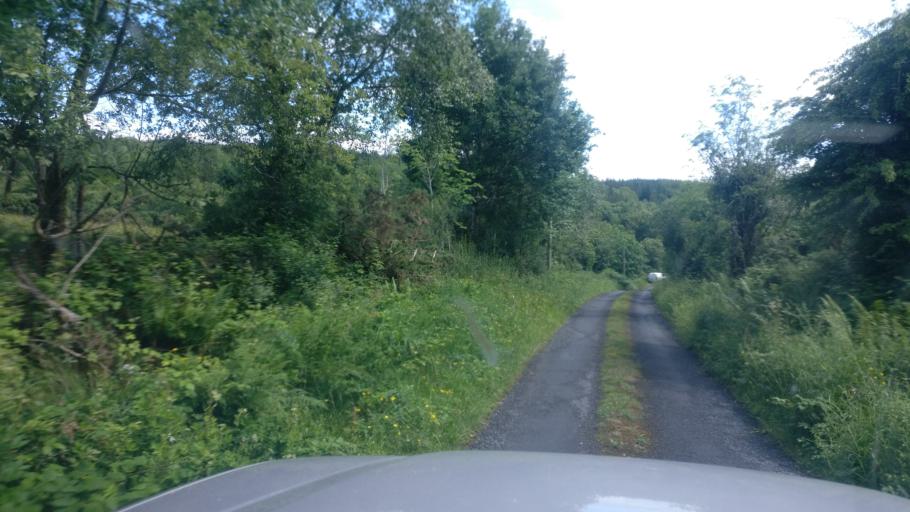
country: IE
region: Connaught
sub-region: County Galway
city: Gort
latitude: 53.0691
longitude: -8.7031
